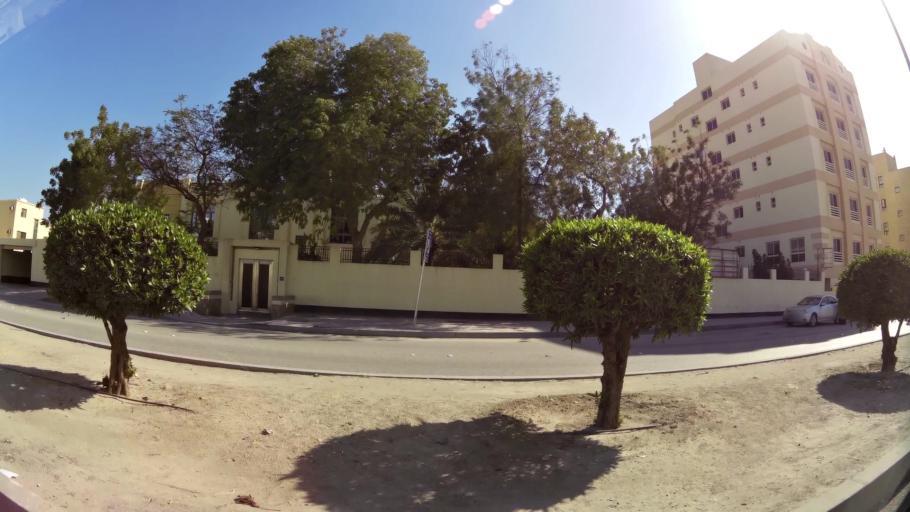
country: BH
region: Manama
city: Manama
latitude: 26.2126
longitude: 50.5677
